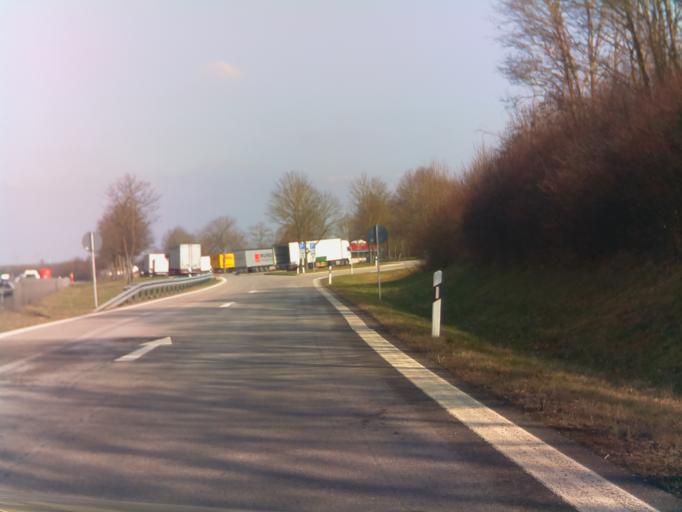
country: DE
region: Baden-Wuerttemberg
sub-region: Regierungsbezirk Stuttgart
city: Motzingen
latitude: 48.4544
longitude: 8.7735
